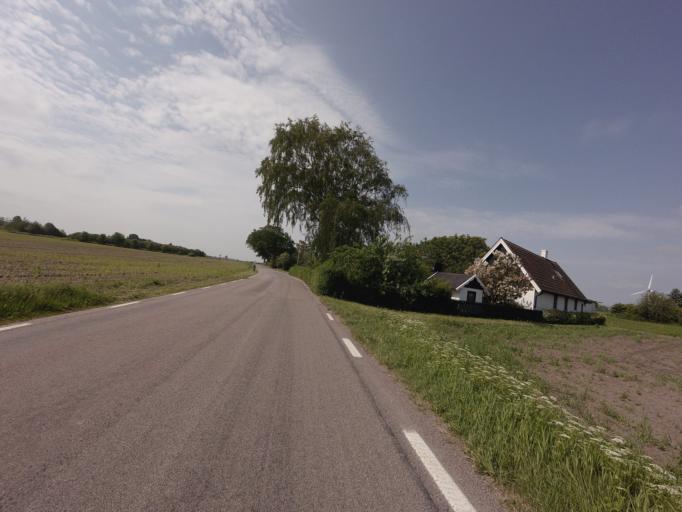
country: SE
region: Skane
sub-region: Helsingborg
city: Odakra
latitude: 56.2009
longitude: 12.7010
